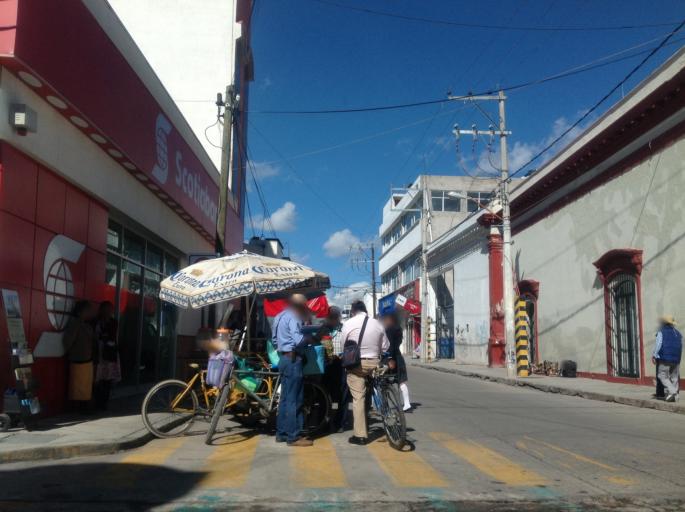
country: MX
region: Oaxaca
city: Ciudad de Huajuapam de Leon
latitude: 17.8056
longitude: -97.7761
